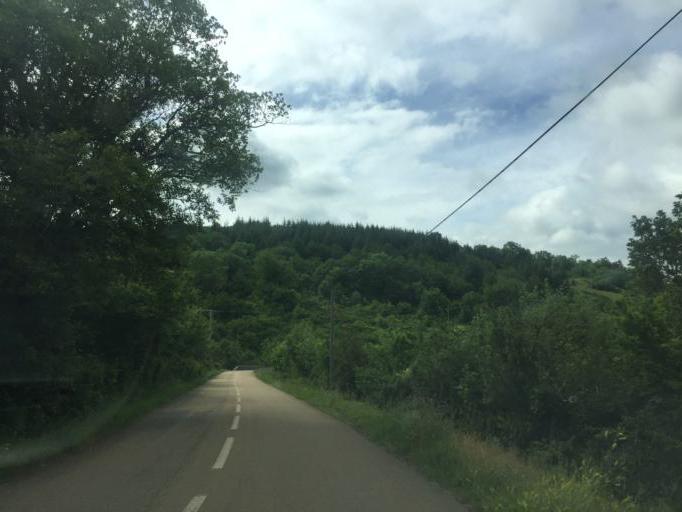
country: FR
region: Rhone-Alpes
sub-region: Departement de l'Ardeche
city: Saint-Priest
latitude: 44.6887
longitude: 4.5489
